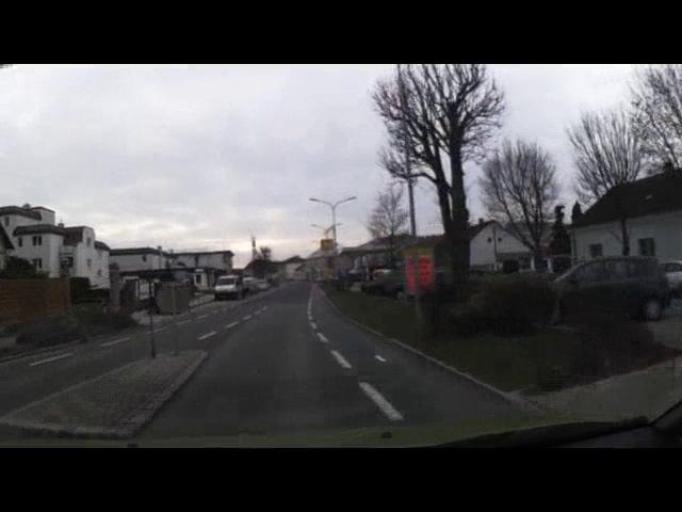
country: AT
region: Burgenland
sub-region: Eisenstadt-Umgebung
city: Neufeld an der Leitha
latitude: 47.8714
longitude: 16.3758
